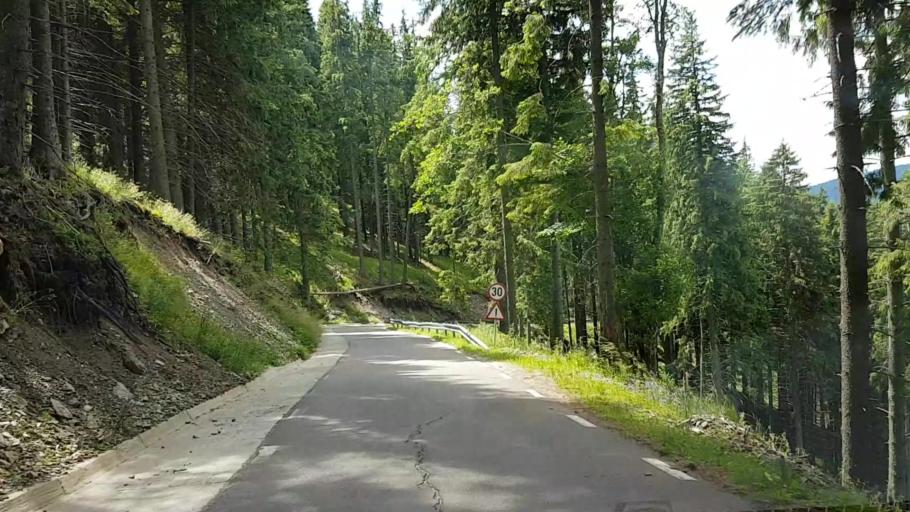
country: RO
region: Suceava
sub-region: Municipiul Campulung Moldovenesc
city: Campulung Moldovenesc
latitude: 47.4422
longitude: 25.5534
